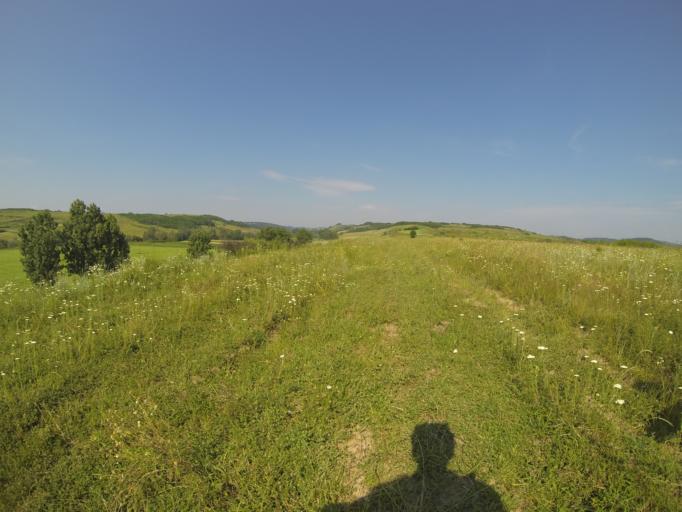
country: RO
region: Gorj
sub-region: Comuna Crusetu
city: Crusetu
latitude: 44.6065
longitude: 23.6769
